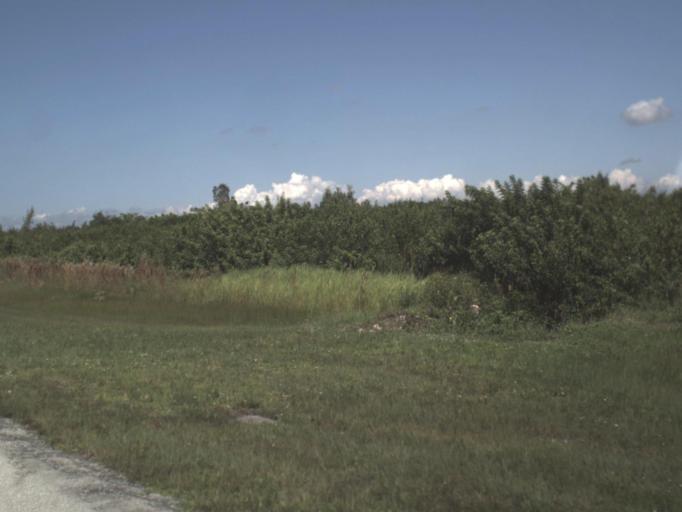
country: US
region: Florida
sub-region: Lee County
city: Pine Island Center
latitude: 26.6153
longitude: -82.0390
